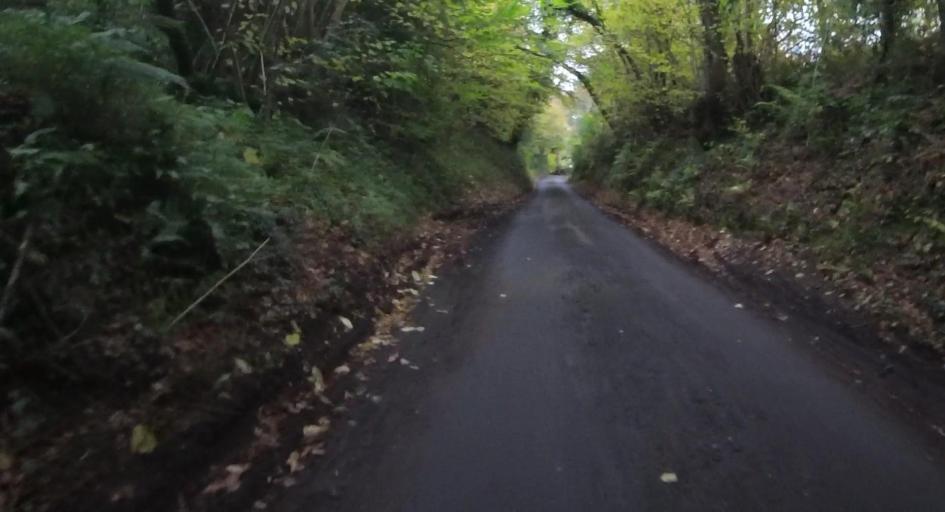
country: GB
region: England
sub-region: Hampshire
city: Lindford
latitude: 51.1292
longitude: -0.8286
